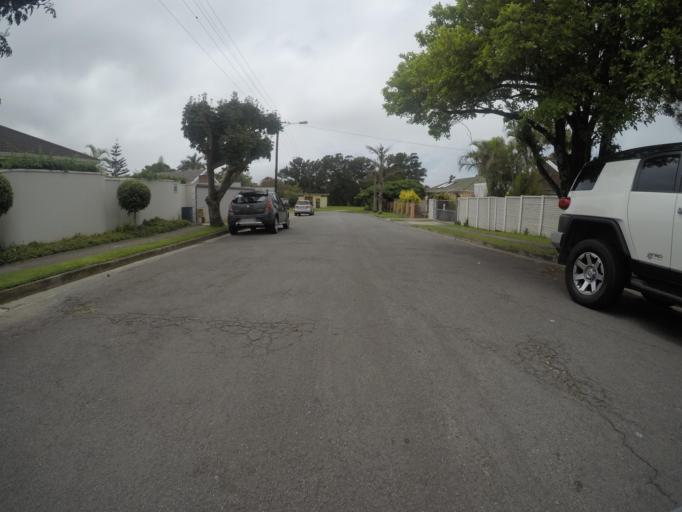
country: ZA
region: Eastern Cape
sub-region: Buffalo City Metropolitan Municipality
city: East London
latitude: -32.9889
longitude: 27.9227
